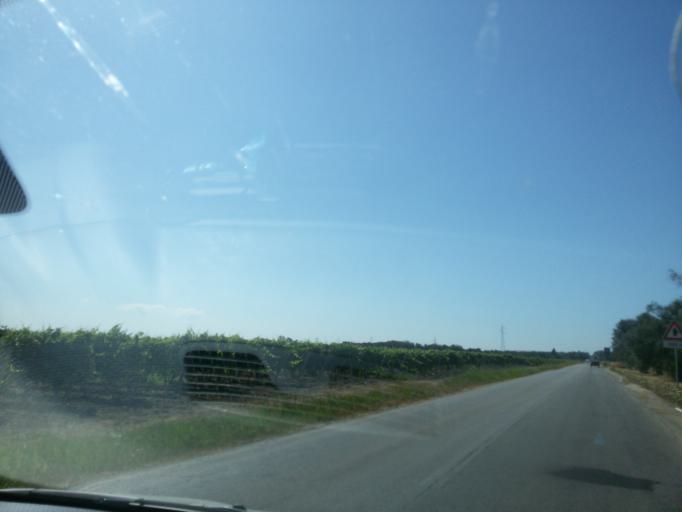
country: IT
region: Apulia
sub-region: Provincia di Brindisi
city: San Donaci
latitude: 40.4636
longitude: 17.9069
